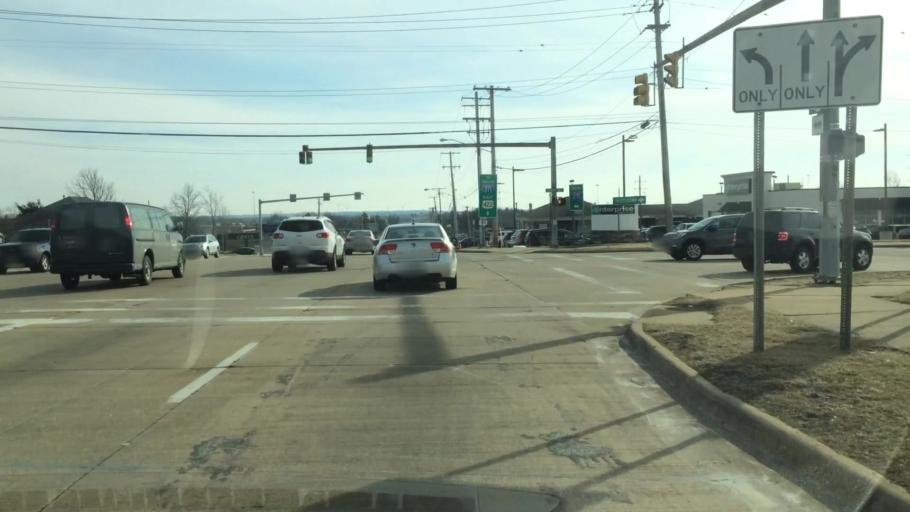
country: US
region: Ohio
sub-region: Cuyahoga County
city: Orange
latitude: 41.4354
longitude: -81.4980
